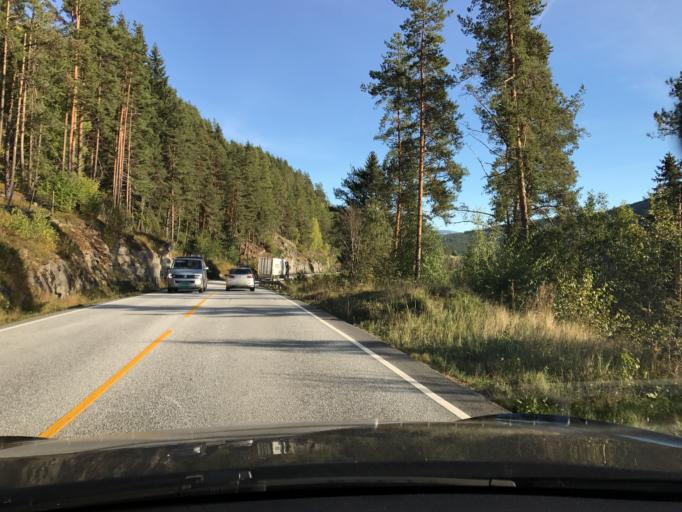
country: NO
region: Sogn og Fjordane
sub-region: Sogndal
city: Sogndalsfjora
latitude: 61.2113
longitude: 7.1465
